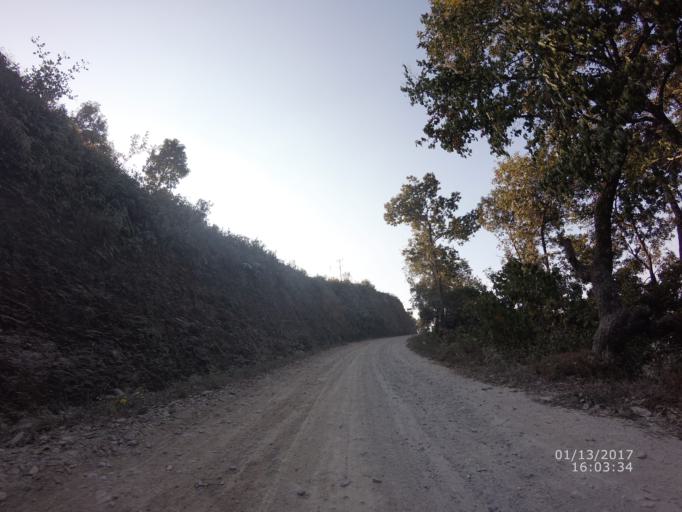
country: NP
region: Western Region
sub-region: Gandaki Zone
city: Pokhara
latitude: 28.1541
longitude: 83.9953
